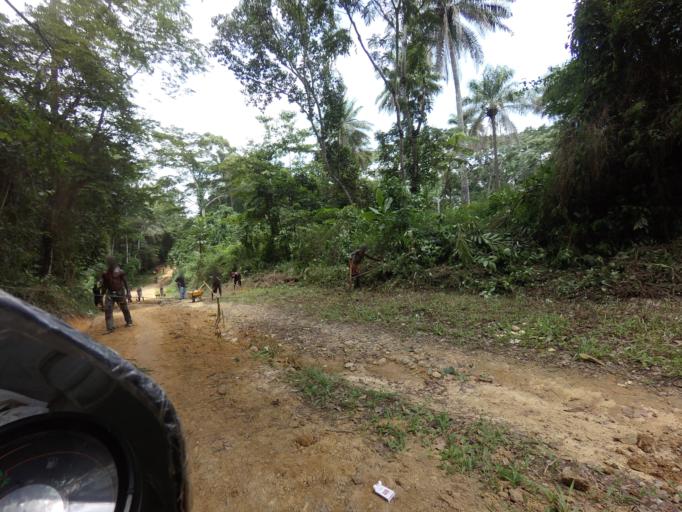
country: SL
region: Eastern Province
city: Kailahun
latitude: 8.3581
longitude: -10.7137
